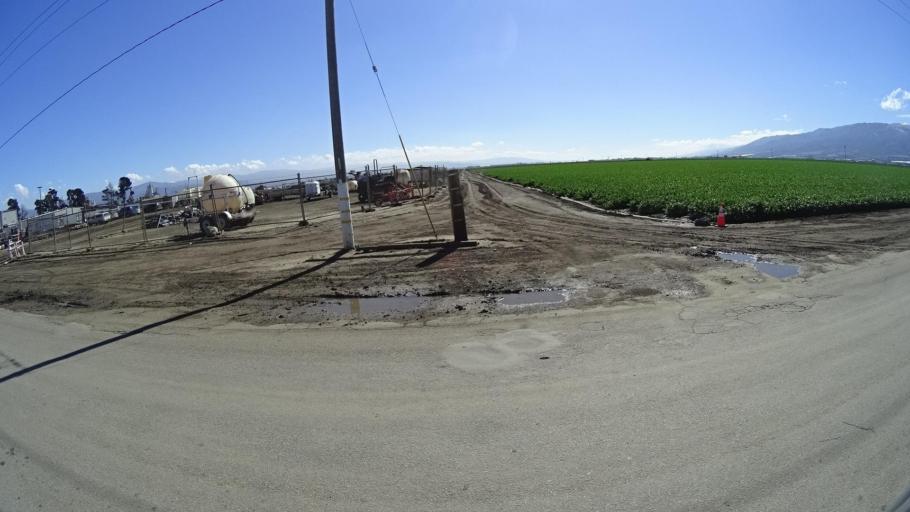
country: US
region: California
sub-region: Monterey County
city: Salinas
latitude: 36.6438
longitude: -121.6352
